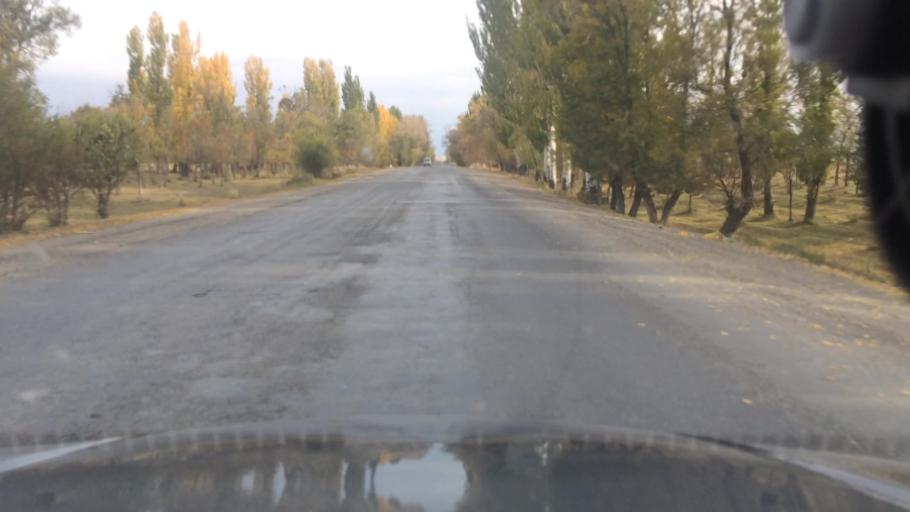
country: KG
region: Ysyk-Koel
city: Karakol
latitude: 42.5411
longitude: 78.3848
